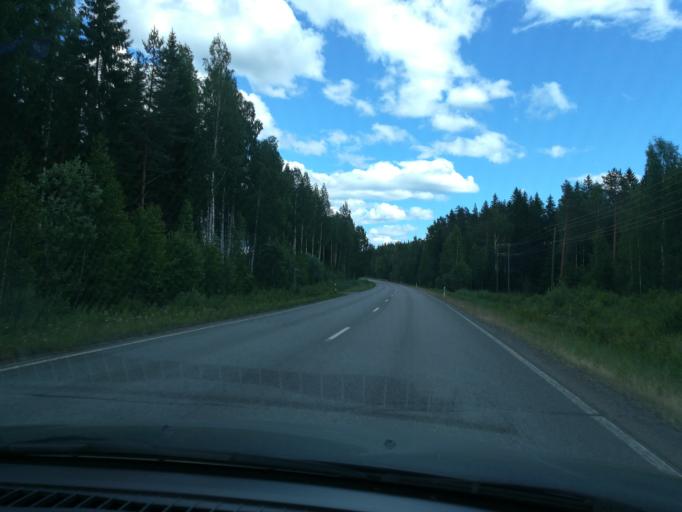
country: FI
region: Southern Savonia
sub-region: Mikkeli
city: Hirvensalmi
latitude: 61.6695
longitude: 26.8661
